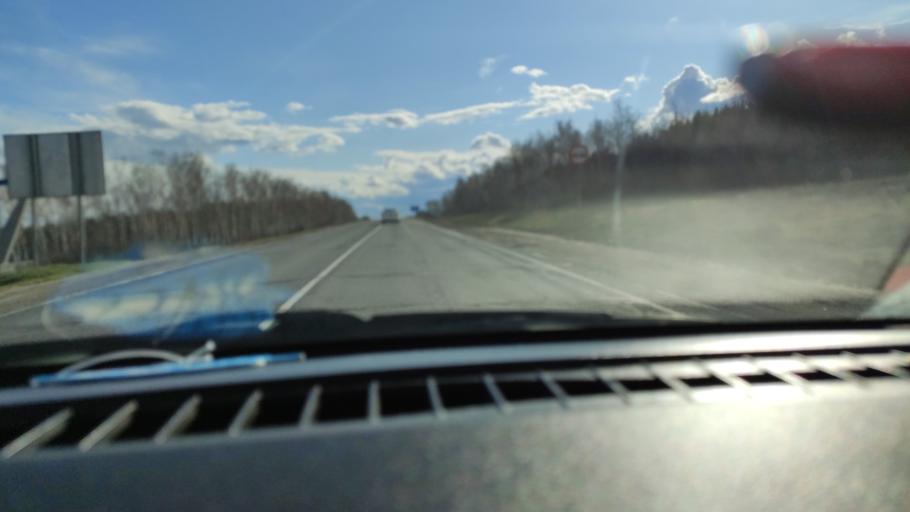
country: RU
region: Saratov
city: Sennoy
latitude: 52.1168
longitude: 46.8392
